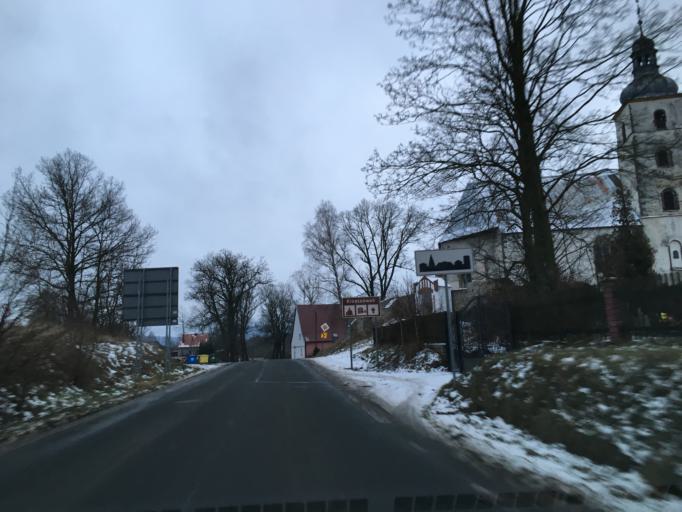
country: PL
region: Lower Silesian Voivodeship
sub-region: Powiat kamiennogorski
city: Krzeszow
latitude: 50.7207
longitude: 16.0862
